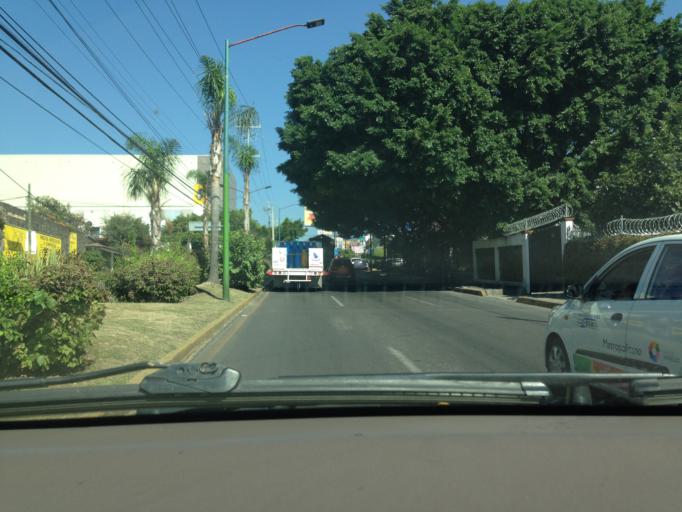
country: MX
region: Morelos
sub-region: Cuernavaca
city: Fraccionamiento Lomas de Ahuatlan
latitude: 18.9533
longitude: -99.2361
